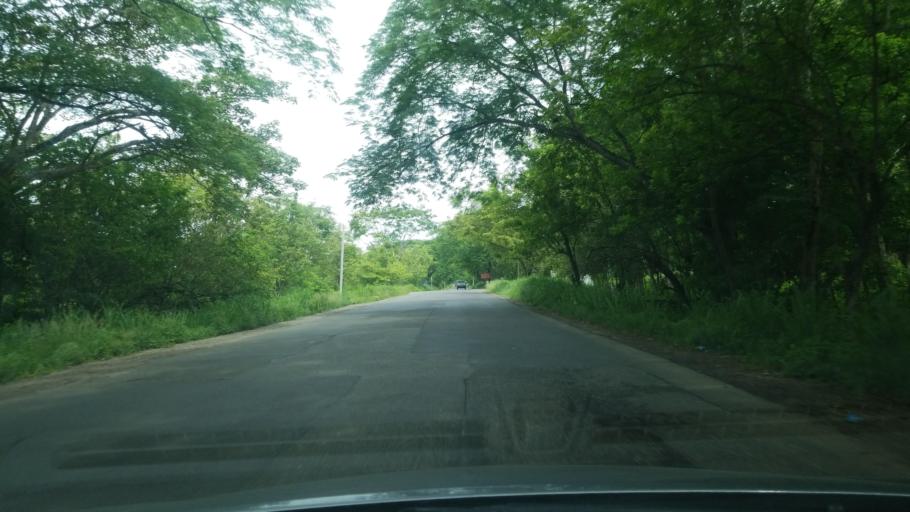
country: HN
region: Santa Barbara
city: Camalote
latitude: 15.3302
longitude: -88.3332
